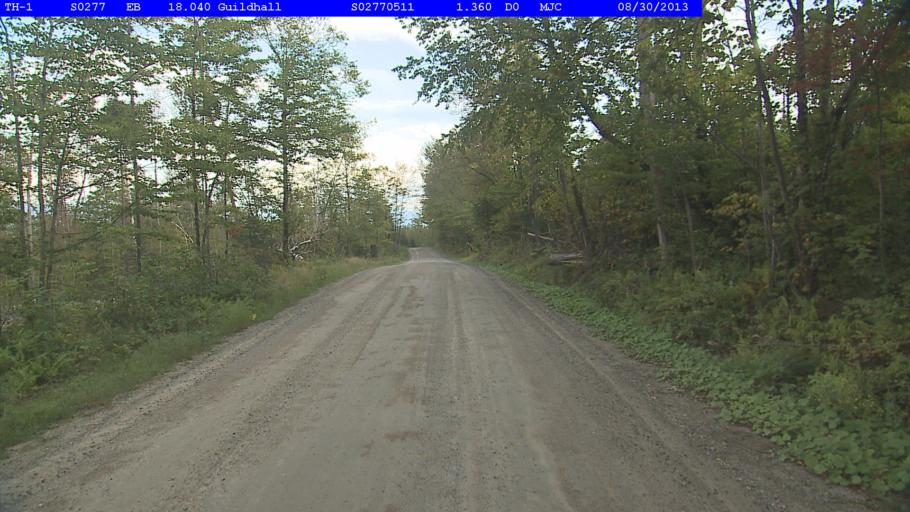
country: US
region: Vermont
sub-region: Essex County
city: Guildhall
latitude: 44.5671
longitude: -71.6450
